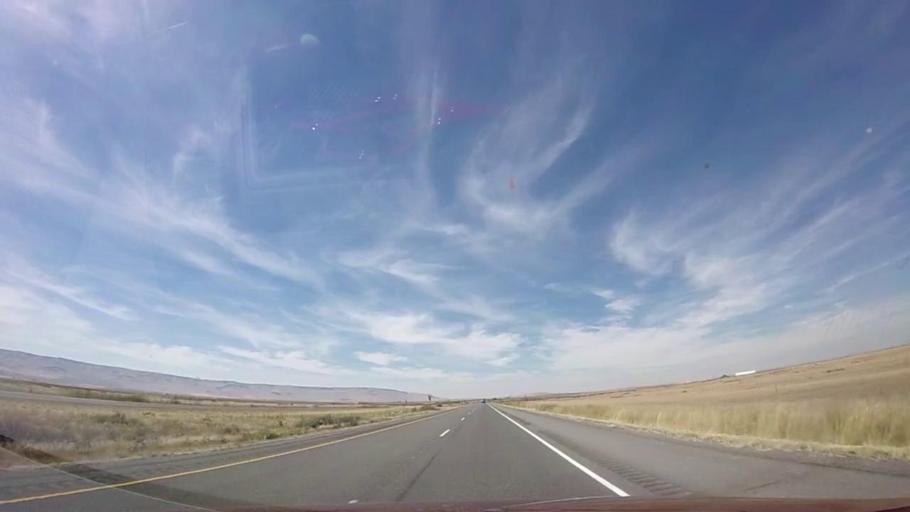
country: US
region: Idaho
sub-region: Minidoka County
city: Rupert
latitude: 42.4080
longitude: -113.3105
